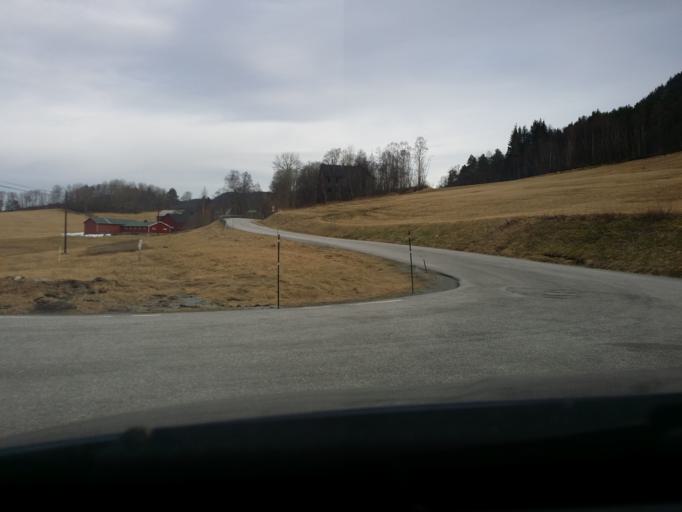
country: NO
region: More og Romsdal
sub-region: Aure
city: Aure
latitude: 63.1304
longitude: 8.5195
